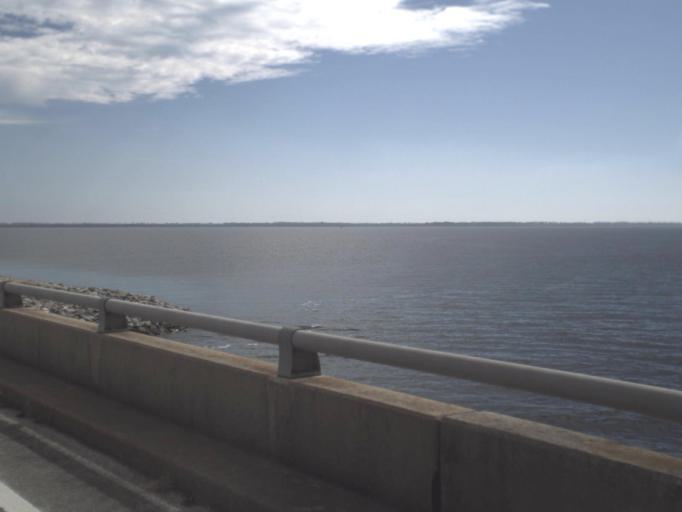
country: US
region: Florida
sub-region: Brevard County
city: Port Saint John
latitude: 28.5272
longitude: -80.7595
